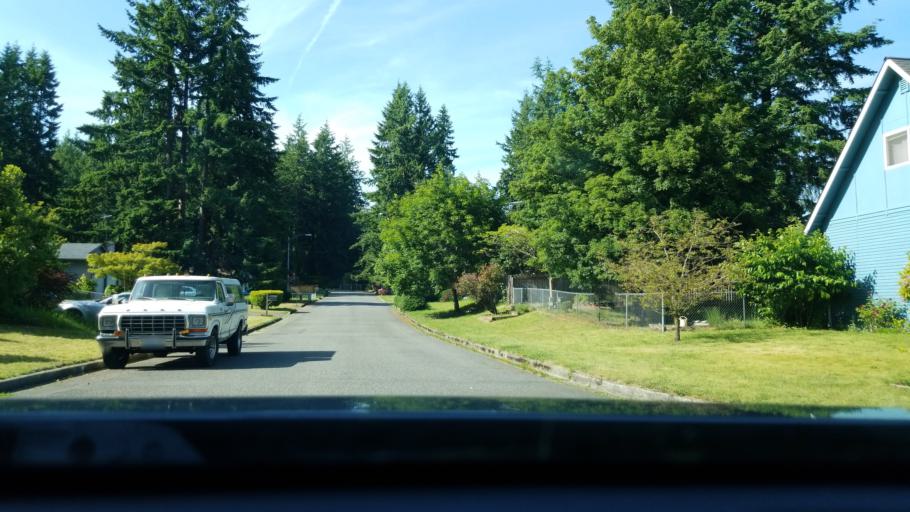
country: US
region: Washington
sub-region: King County
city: Fairwood
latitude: 47.4765
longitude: -122.1457
